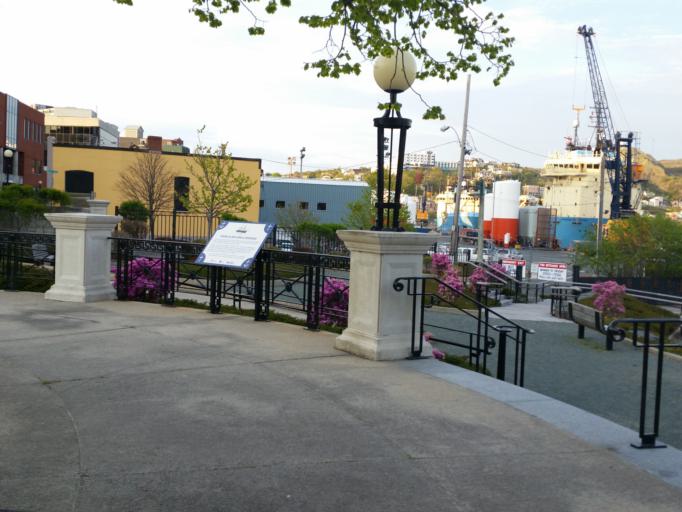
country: CA
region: Newfoundland and Labrador
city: St. John's
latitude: 47.5672
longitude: -52.7033
